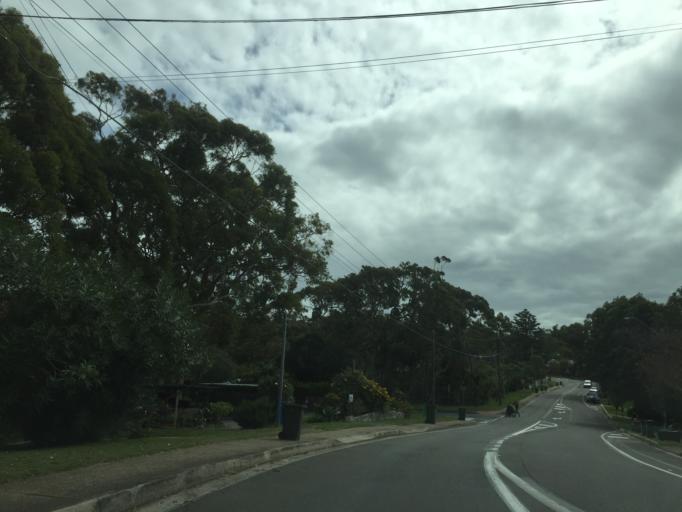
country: AU
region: New South Wales
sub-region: Pittwater
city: Warriewood
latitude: -33.6990
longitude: 151.2880
